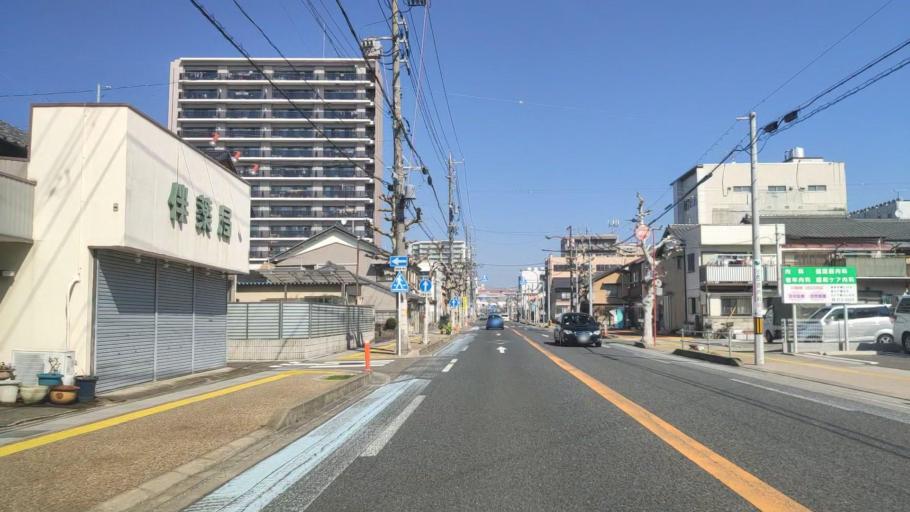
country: JP
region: Gifu
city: Gifu-shi
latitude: 35.4035
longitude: 136.7543
